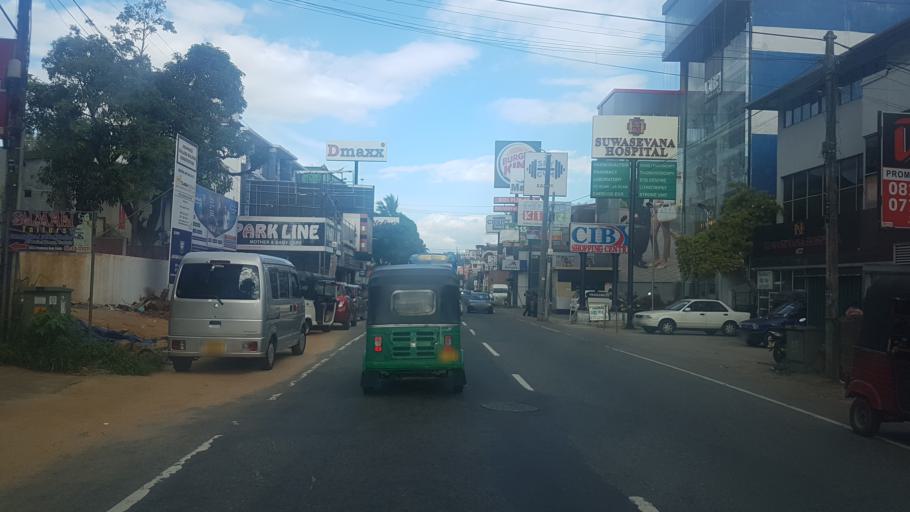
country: LK
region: Central
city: Kandy
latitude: 7.2817
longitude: 80.6211
